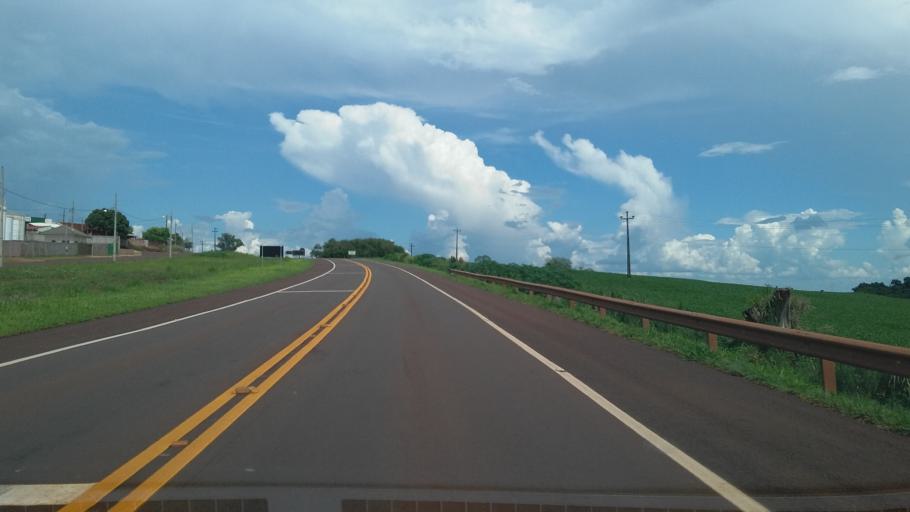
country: BR
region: Parana
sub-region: Corbelia
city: Corbelia
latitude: -24.5575
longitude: -52.9965
